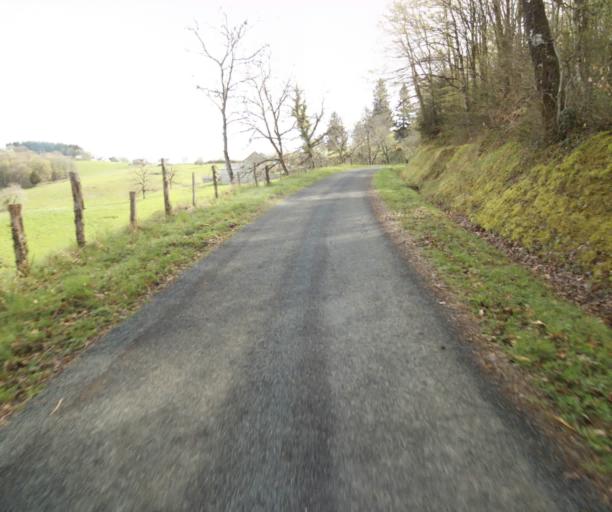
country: FR
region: Limousin
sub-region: Departement de la Correze
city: Laguenne
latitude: 45.2500
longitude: 1.8015
